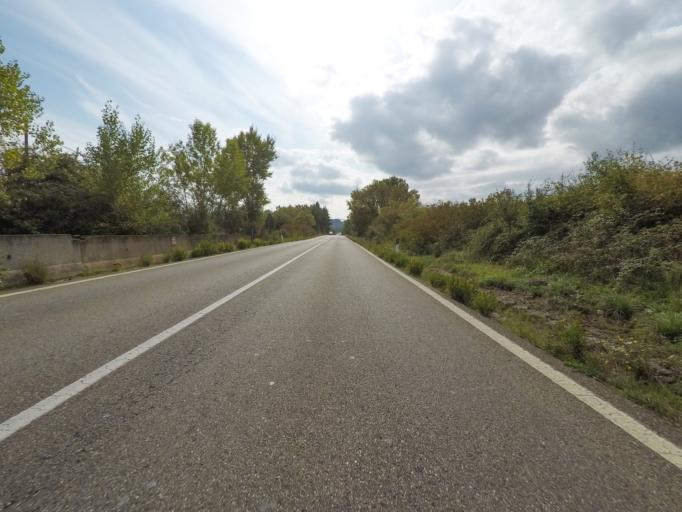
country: IT
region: Tuscany
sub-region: Provincia di Siena
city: Murlo
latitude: 43.1256
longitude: 11.2961
